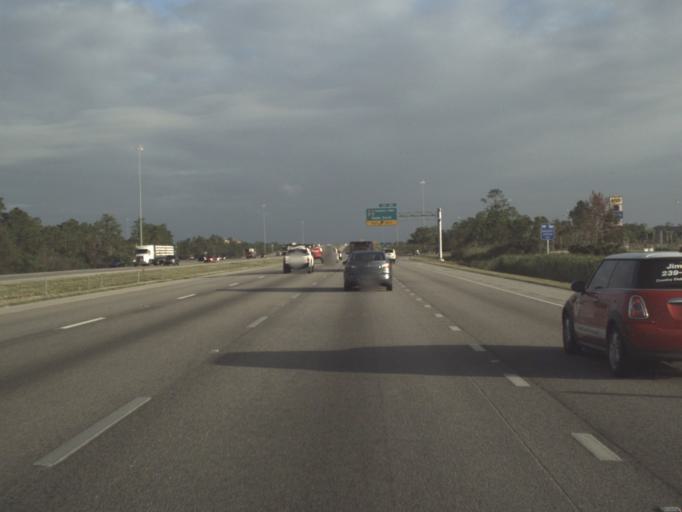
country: US
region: Florida
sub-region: Lee County
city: Gateway
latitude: 26.5403
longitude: -81.7947
